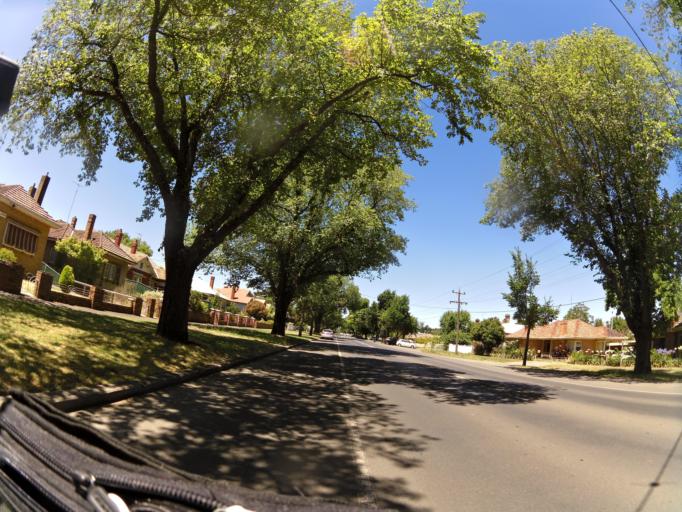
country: AU
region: Victoria
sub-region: Ballarat North
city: Newington
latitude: -37.5634
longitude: 143.8327
